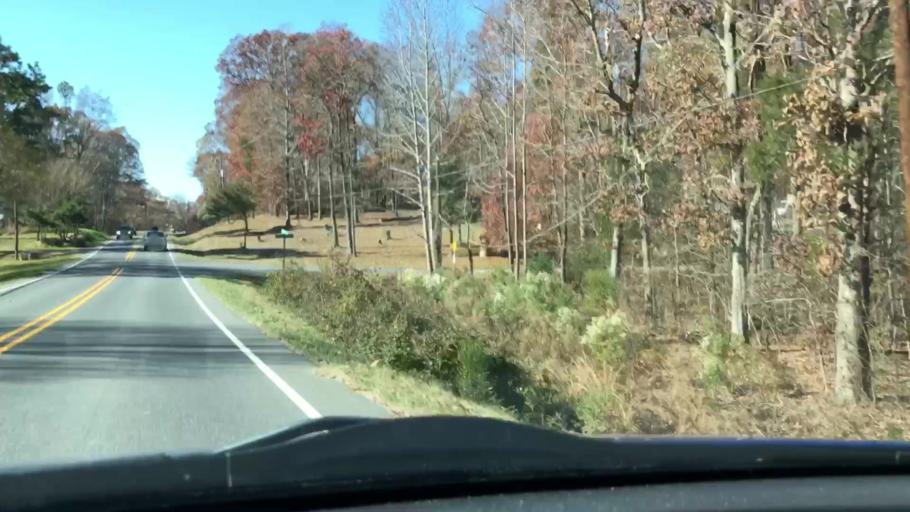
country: US
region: North Carolina
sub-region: Randolph County
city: Asheboro
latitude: 35.6766
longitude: -79.8821
